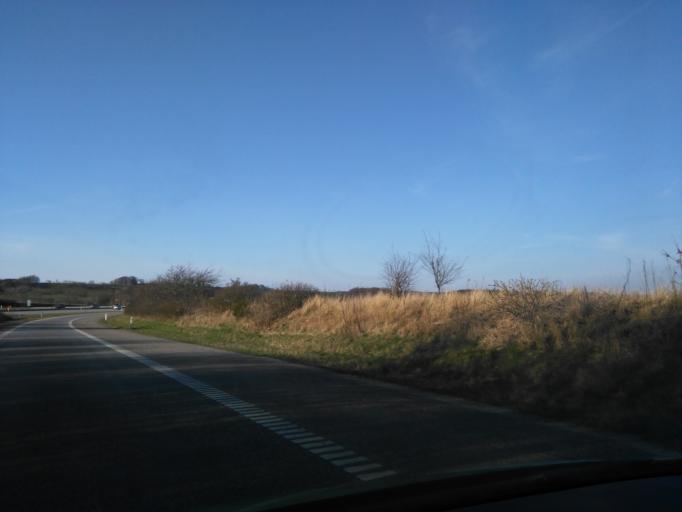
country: DK
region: Central Jutland
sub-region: Skanderborg Kommune
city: Skanderborg
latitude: 56.0296
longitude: 9.8830
